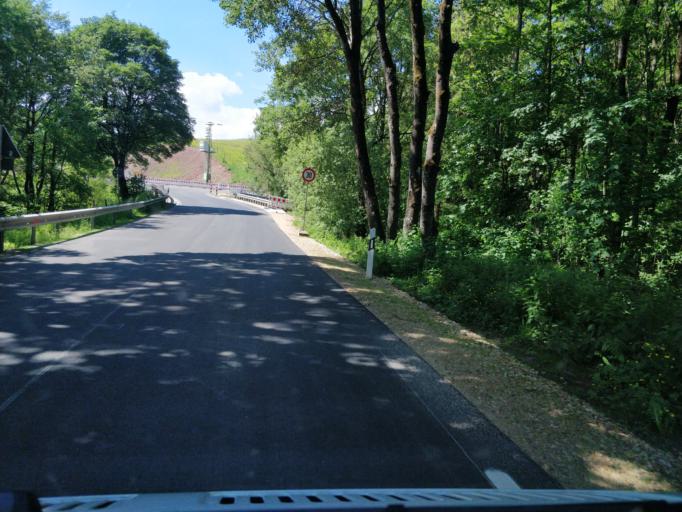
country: DE
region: Rheinland-Pfalz
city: Hallschlag
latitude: 50.3632
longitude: 6.4508
